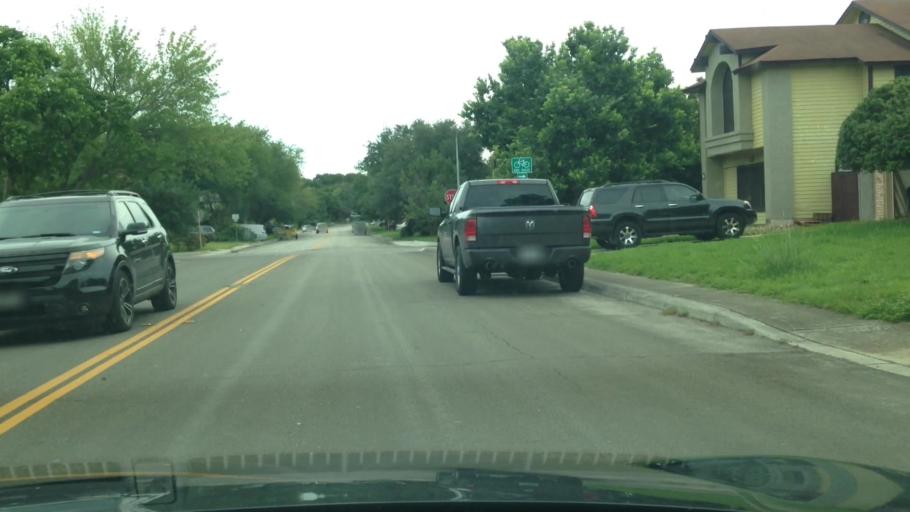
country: US
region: Texas
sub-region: Bexar County
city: Hollywood Park
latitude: 29.5731
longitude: -98.4284
